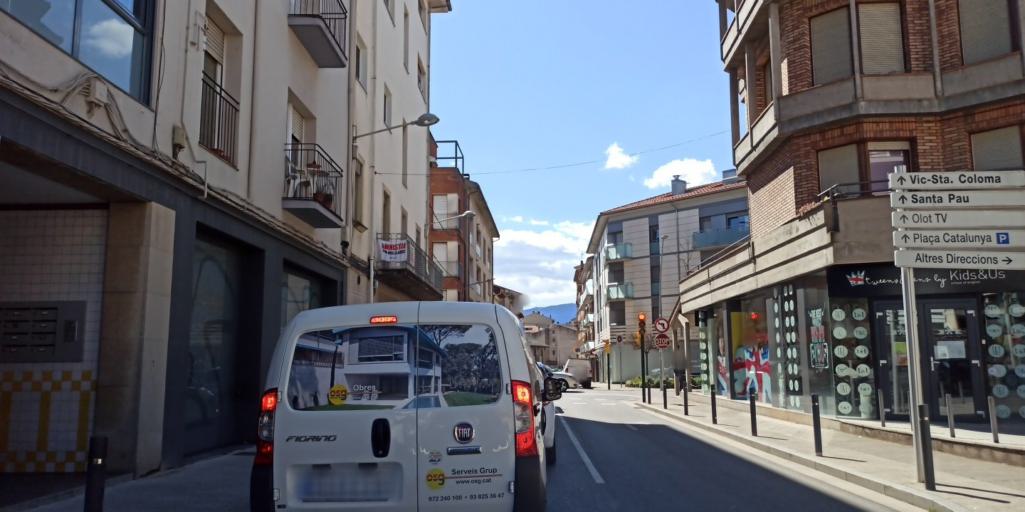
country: ES
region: Catalonia
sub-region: Provincia de Girona
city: MeteOlot
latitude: 42.1820
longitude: 2.4840
